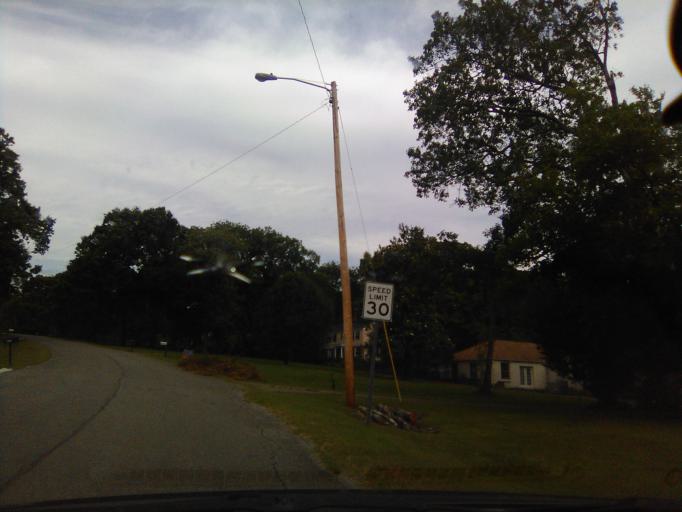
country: US
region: Tennessee
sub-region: Davidson County
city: Belle Meade
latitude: 36.1057
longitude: -86.8886
